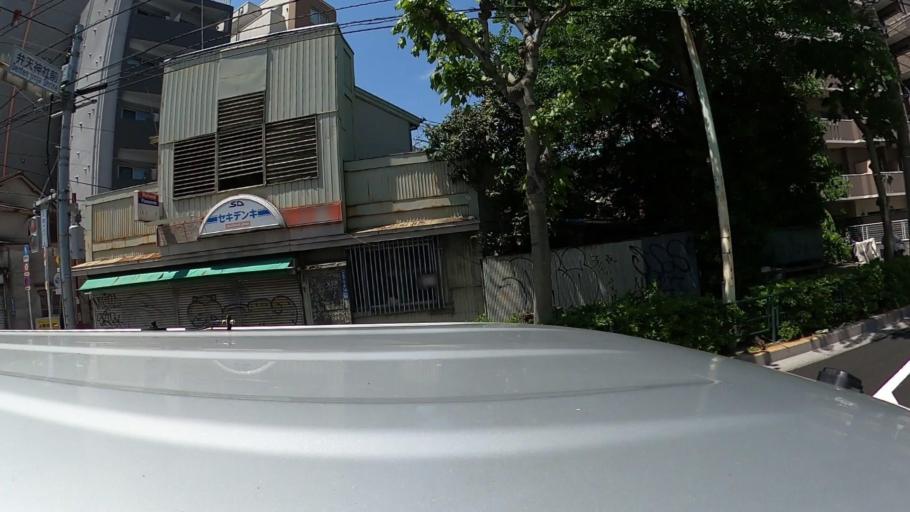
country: JP
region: Kanagawa
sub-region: Kawasaki-shi
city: Kawasaki
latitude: 35.5675
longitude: 139.7359
